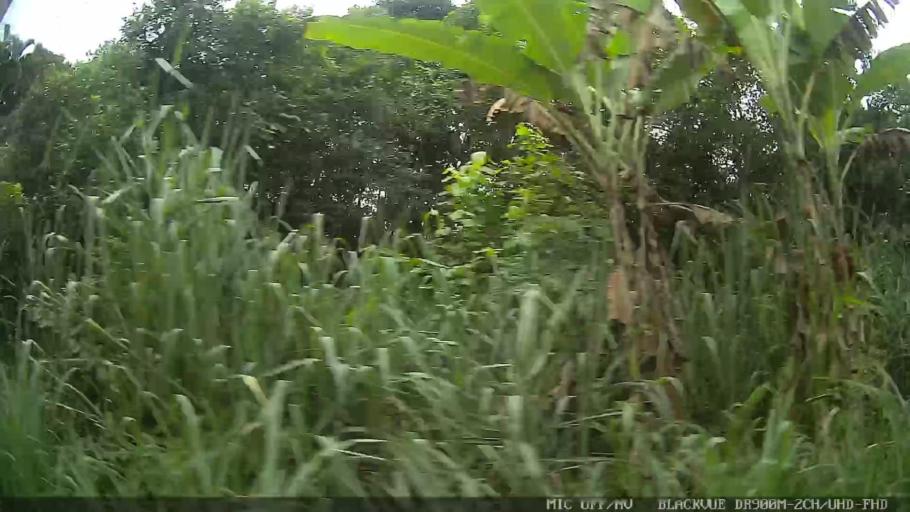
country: BR
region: Sao Paulo
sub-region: Iguape
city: Iguape
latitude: -24.6906
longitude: -47.5255
